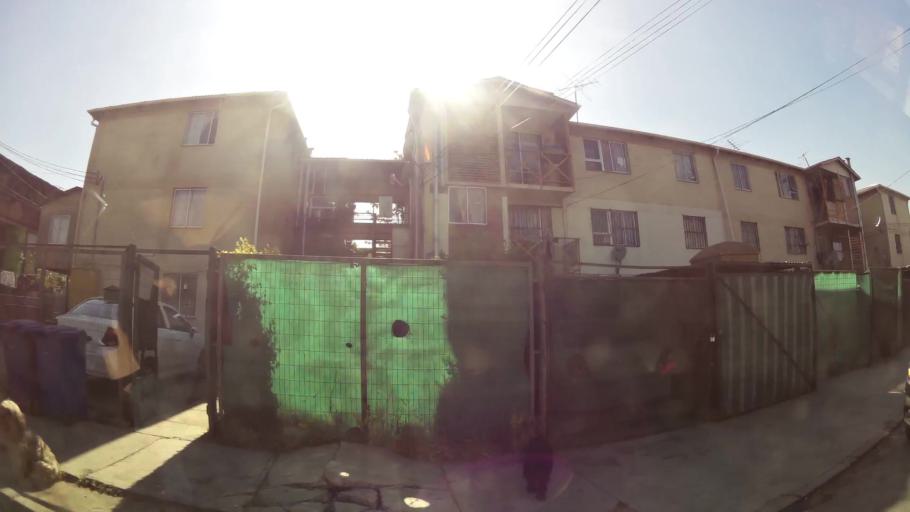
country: CL
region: Santiago Metropolitan
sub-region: Provincia de Maipo
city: San Bernardo
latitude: -33.5643
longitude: -70.7051
